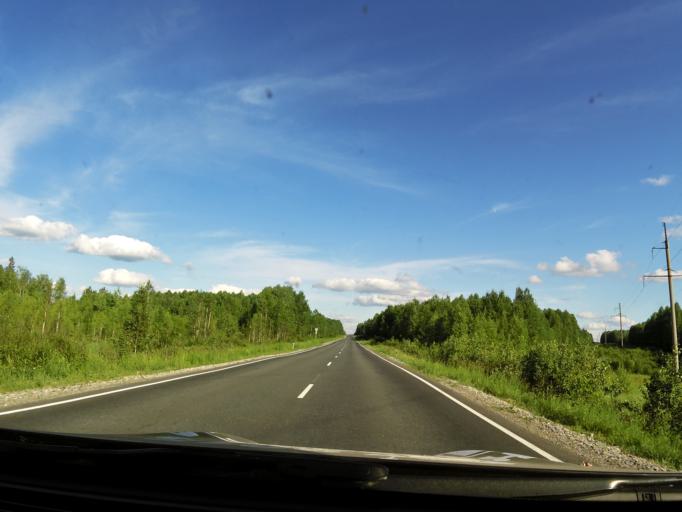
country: RU
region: Kirov
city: Chernaya Kholunitsa
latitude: 58.8062
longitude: 51.8473
